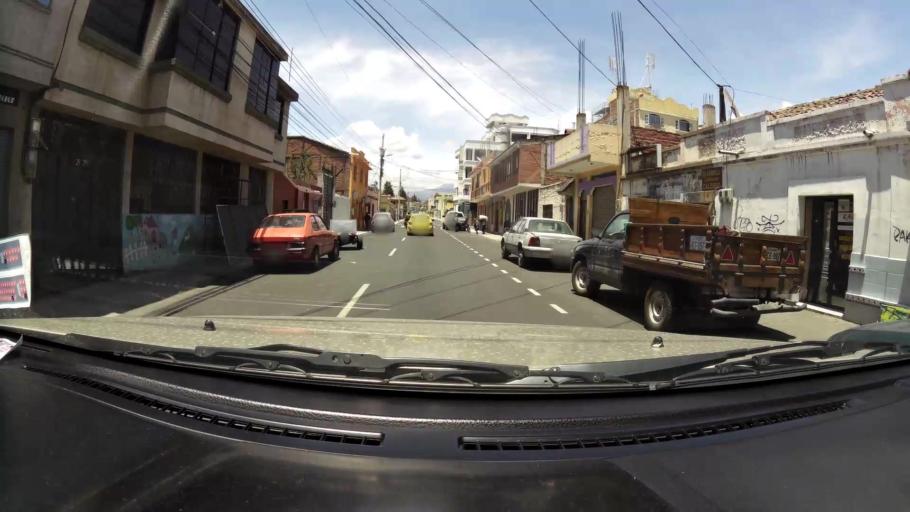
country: EC
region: Chimborazo
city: Riobamba
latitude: -1.6656
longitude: -78.6501
